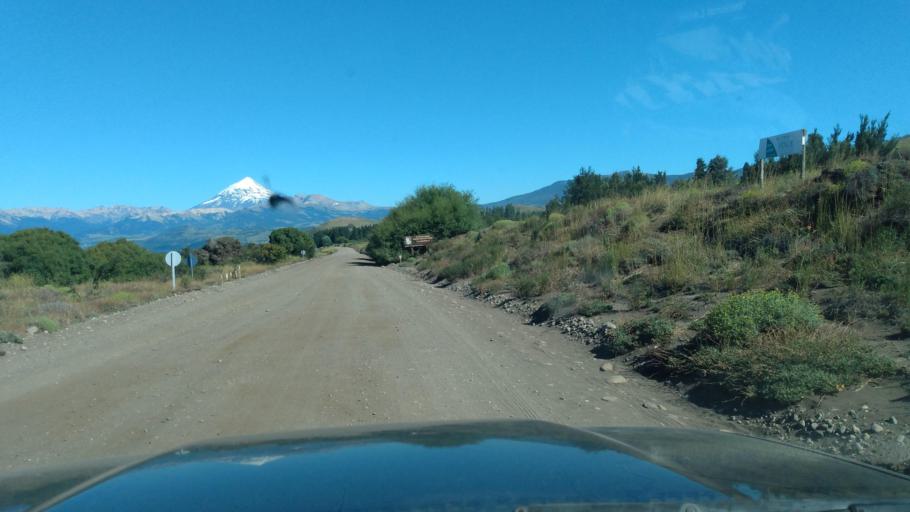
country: AR
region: Neuquen
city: Junin de los Andes
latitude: -39.7901
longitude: -71.2179
